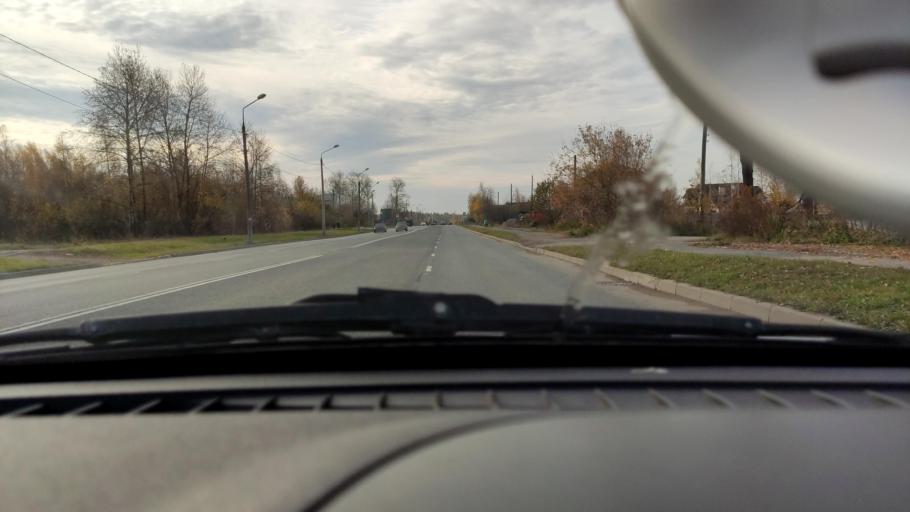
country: RU
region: Perm
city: Polazna
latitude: 58.1192
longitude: 56.4028
